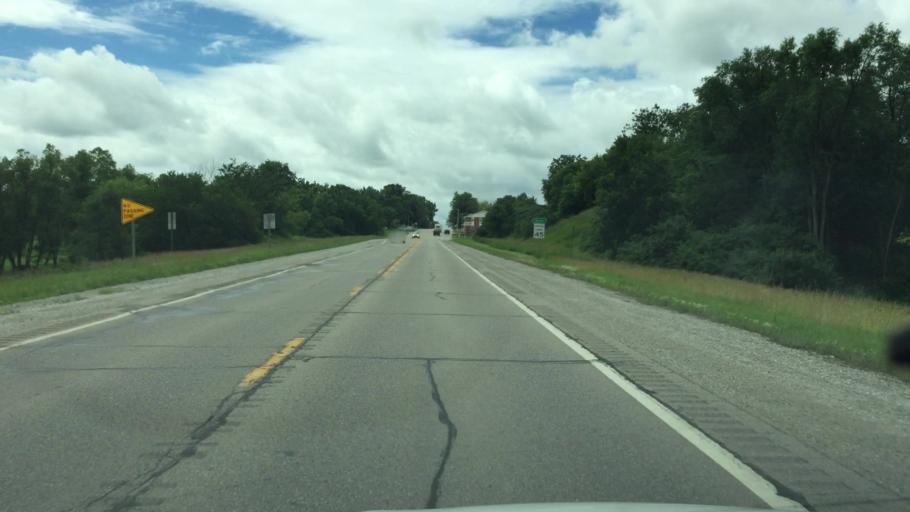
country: US
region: Iowa
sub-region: Jasper County
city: Monroe
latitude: 41.5306
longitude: -93.1019
